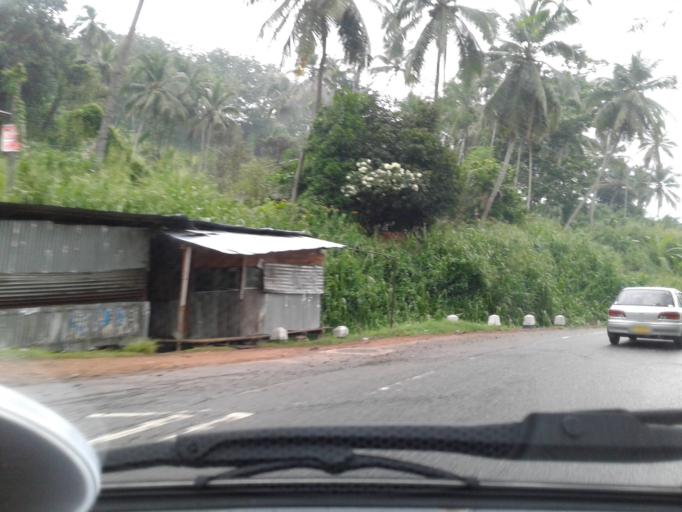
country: LK
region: Central
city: Kadugannawa
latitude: 7.2368
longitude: 80.2690
